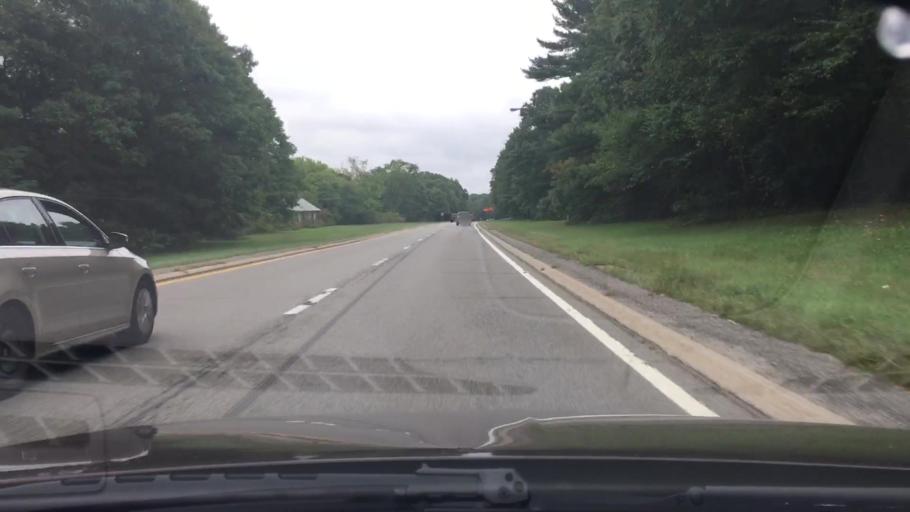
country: US
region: New York
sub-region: Suffolk County
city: Commack
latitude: 40.8249
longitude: -73.3109
